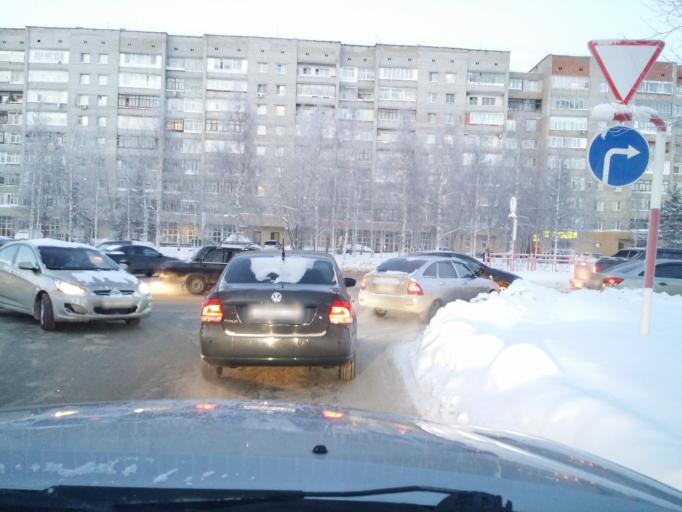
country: RU
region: Khanty-Mansiyskiy Avtonomnyy Okrug
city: Nizhnevartovsk
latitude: 60.9393
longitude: 76.5620
